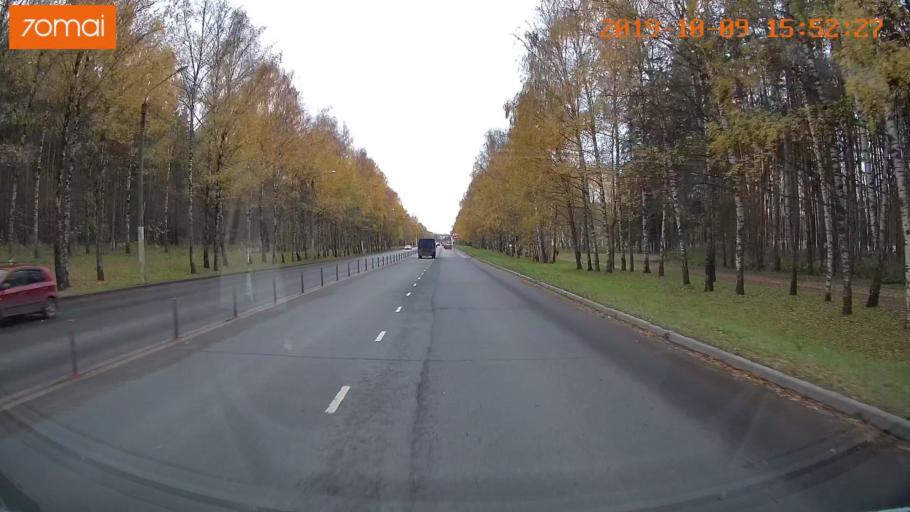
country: RU
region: Kostroma
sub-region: Kostromskoy Rayon
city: Kostroma
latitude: 57.7894
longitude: 40.9671
